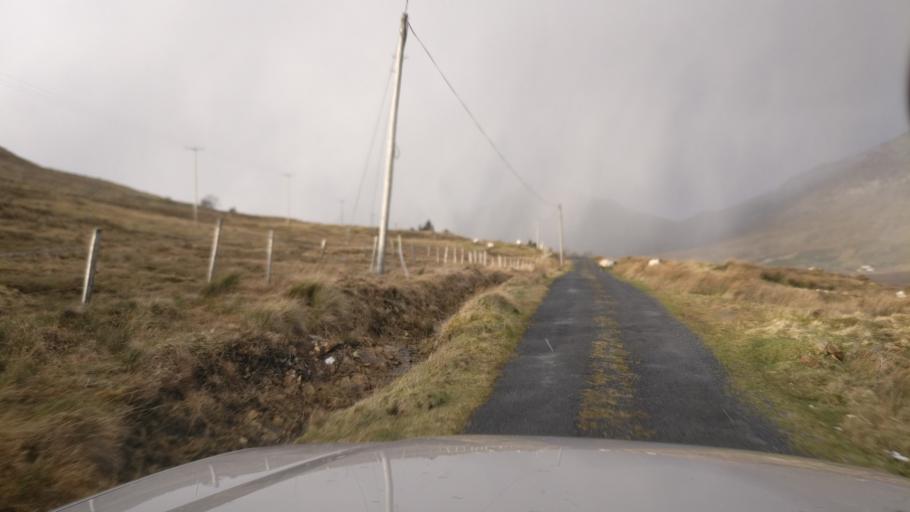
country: IE
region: Connaught
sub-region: County Galway
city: Clifden
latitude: 53.4833
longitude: -9.6968
